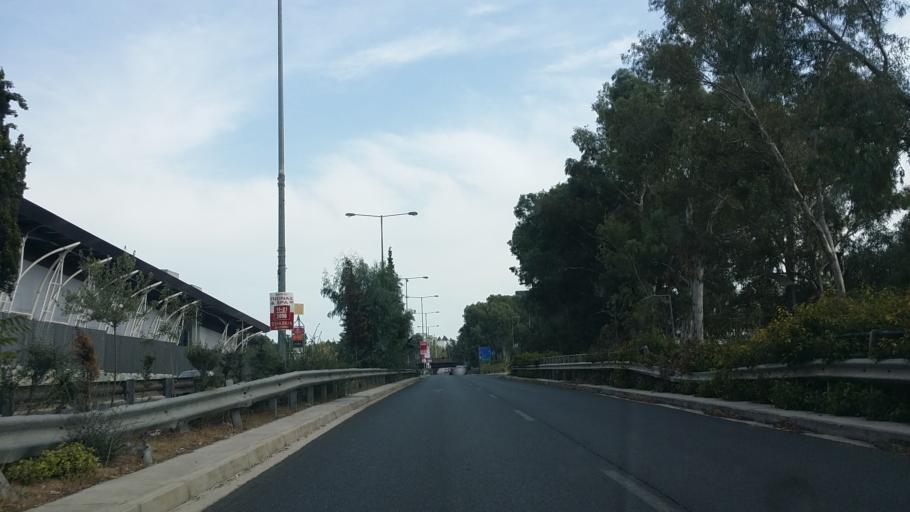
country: GR
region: Attica
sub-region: Nomarchia Athinas
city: Filothei
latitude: 38.0336
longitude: 23.7915
